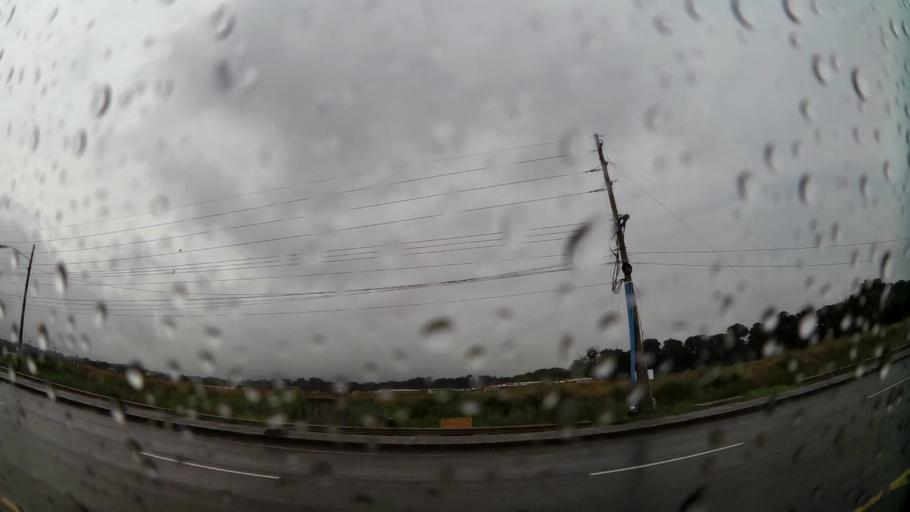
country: PA
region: Colon
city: Arco Iris
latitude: 9.3365
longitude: -79.8852
